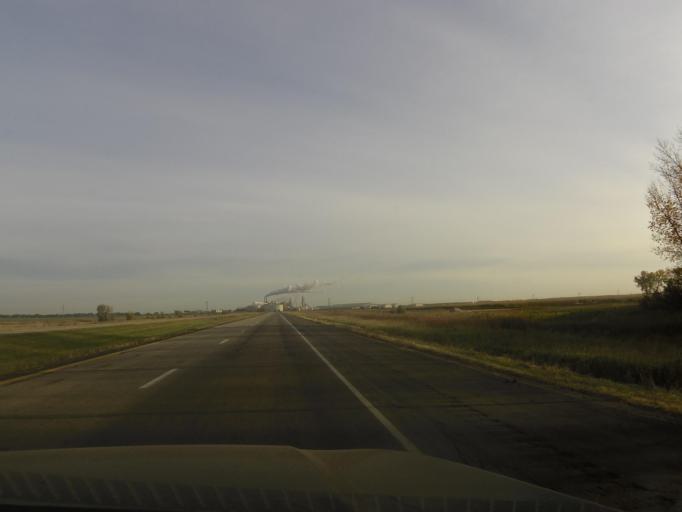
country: US
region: North Dakota
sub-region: Walsh County
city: Grafton
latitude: 48.5777
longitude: -97.1848
